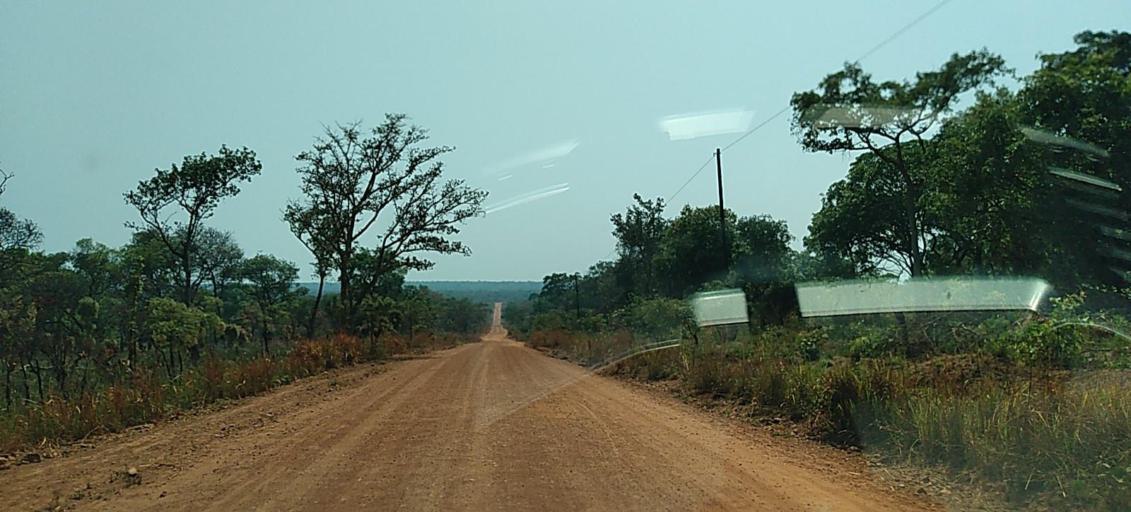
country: ZM
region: North-Western
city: Kansanshi
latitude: -12.0032
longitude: 26.5858
